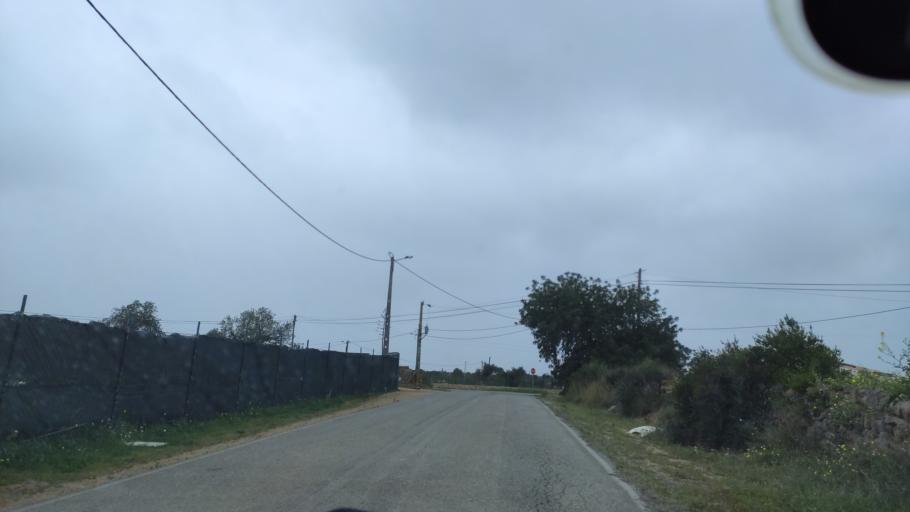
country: PT
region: Faro
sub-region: Faro
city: Santa Barbara de Nexe
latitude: 37.0844
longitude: -7.9210
